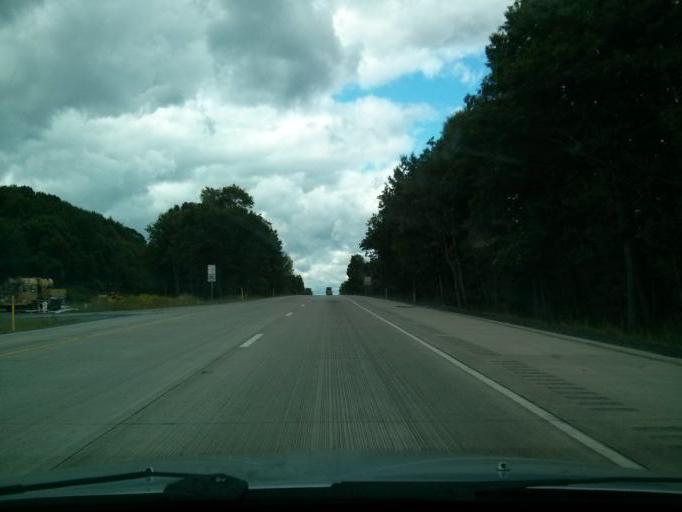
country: US
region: Pennsylvania
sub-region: Jefferson County
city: Reynoldsville
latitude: 41.1526
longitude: -78.9117
